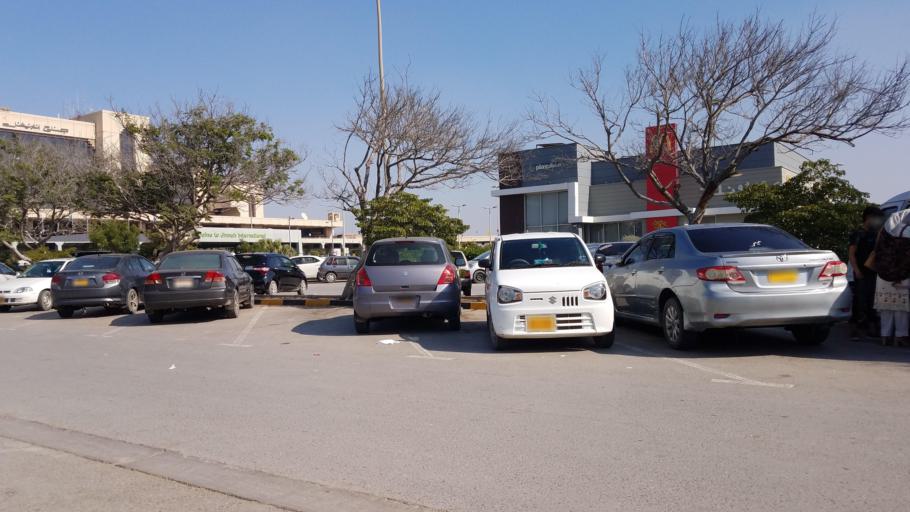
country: PK
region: Sindh
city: Malir Cantonment
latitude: 24.8987
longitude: 67.1681
